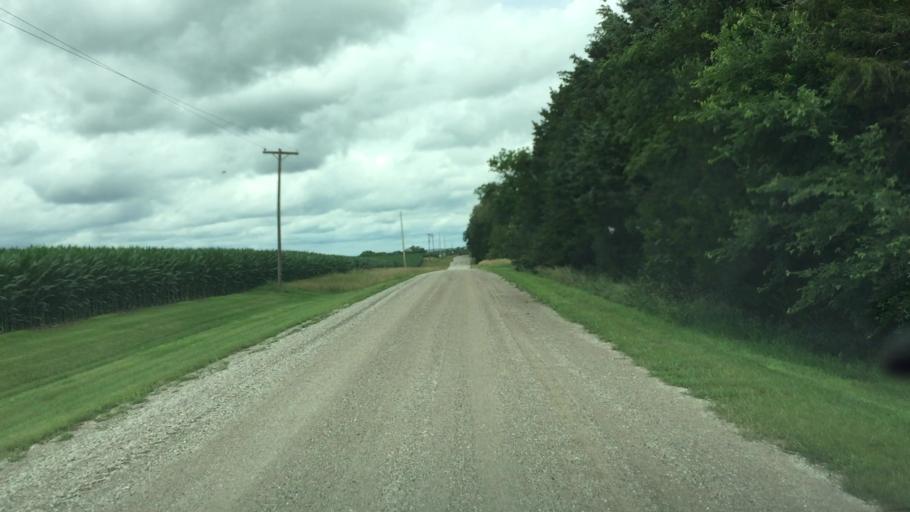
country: US
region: Iowa
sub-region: Jasper County
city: Monroe
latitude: 41.5925
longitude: -93.1160
